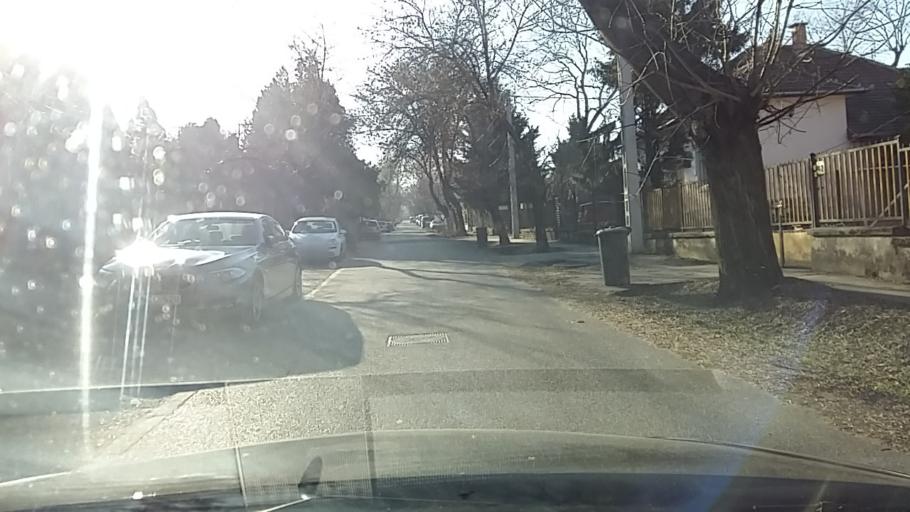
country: HU
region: Budapest
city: Budapest XVI. keruelet
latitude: 47.5211
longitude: 19.1701
